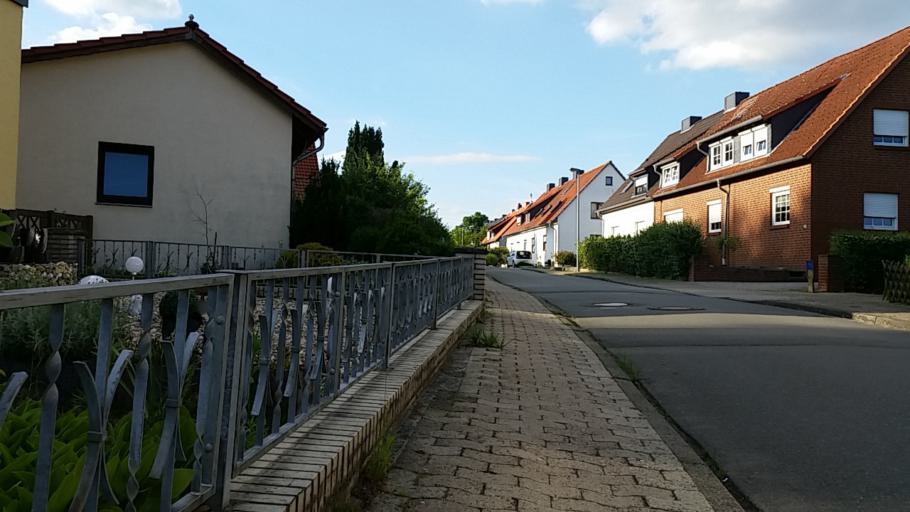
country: DE
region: Lower Saxony
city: Weyhausen
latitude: 52.3903
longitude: 10.7177
